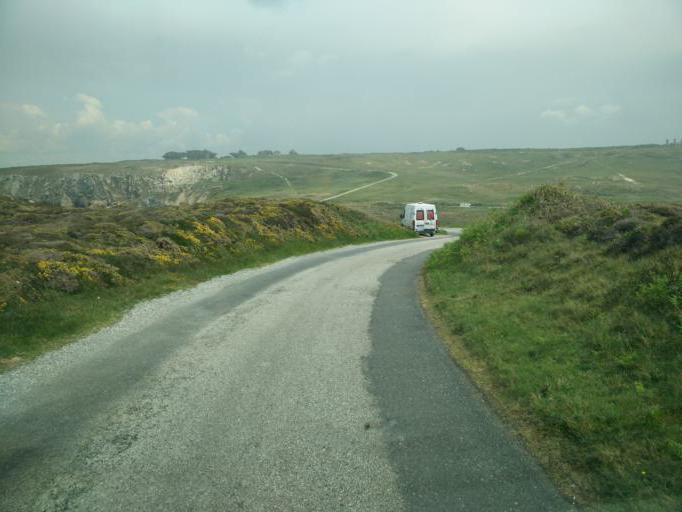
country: FR
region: Brittany
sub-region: Departement du Finistere
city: Camaret-sur-Mer
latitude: 48.2792
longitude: -4.6206
